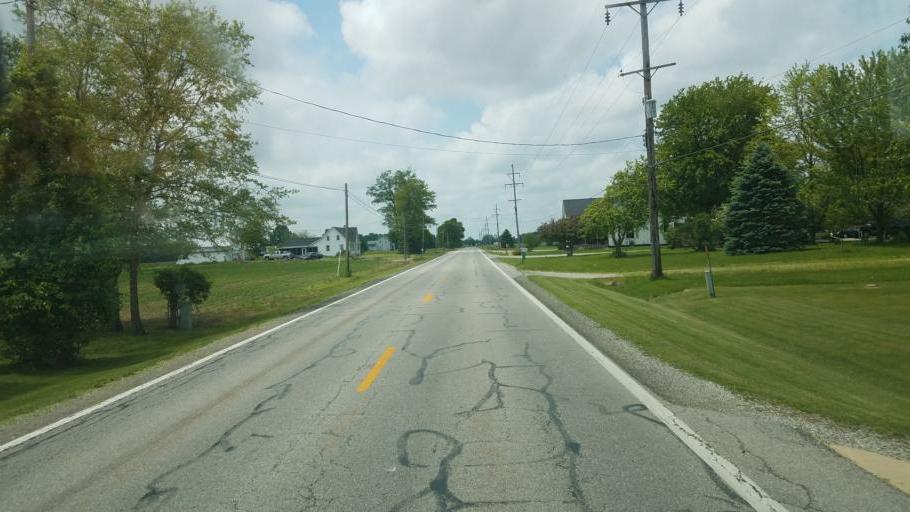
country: US
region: Ohio
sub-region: Marion County
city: Prospect
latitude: 40.4502
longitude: -83.2114
